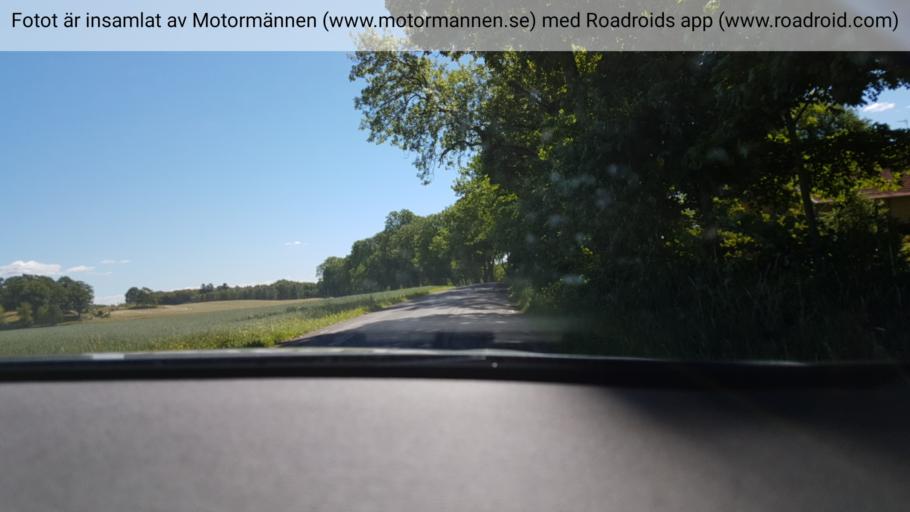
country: SE
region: Vaestra Goetaland
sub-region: Tidaholms Kommun
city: Tidaholm
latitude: 58.1962
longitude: 13.8206
